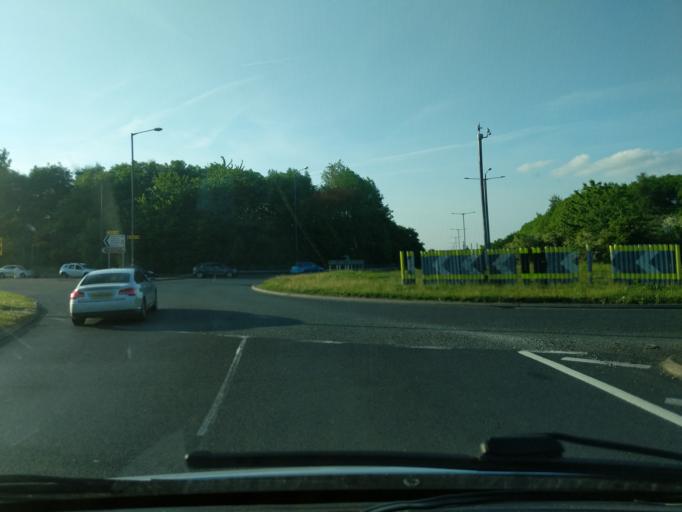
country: GB
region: England
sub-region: St. Helens
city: St Helens
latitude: 53.4281
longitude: -2.7400
